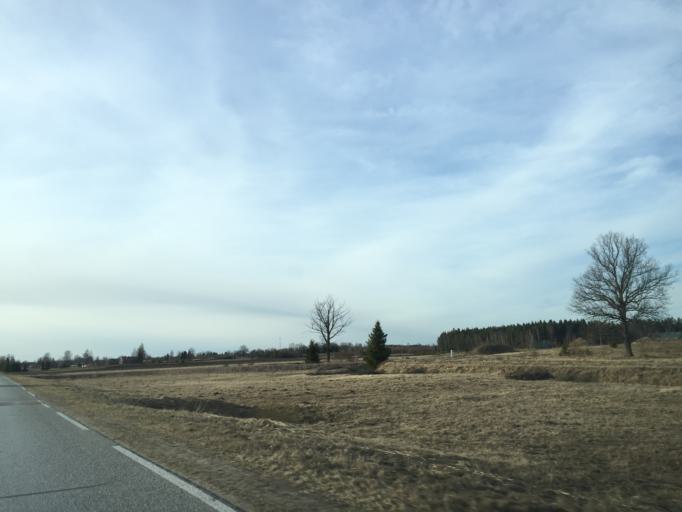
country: LV
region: Krimulda
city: Ragana
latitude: 57.1727
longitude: 24.7287
